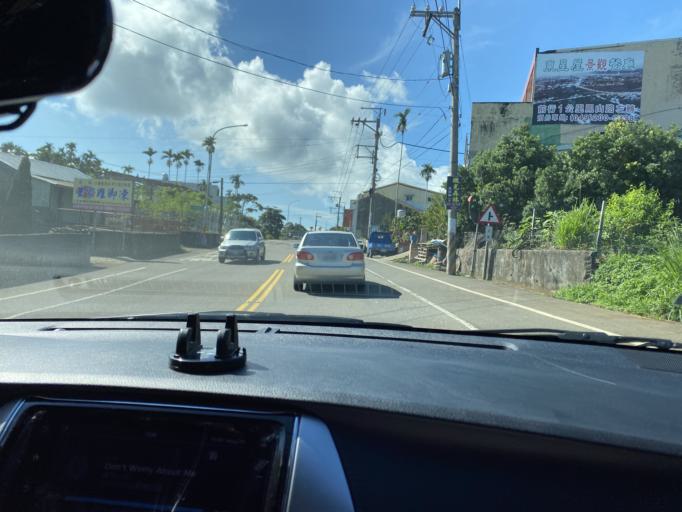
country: TW
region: Taiwan
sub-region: Nantou
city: Nantou
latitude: 23.9443
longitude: 120.6359
